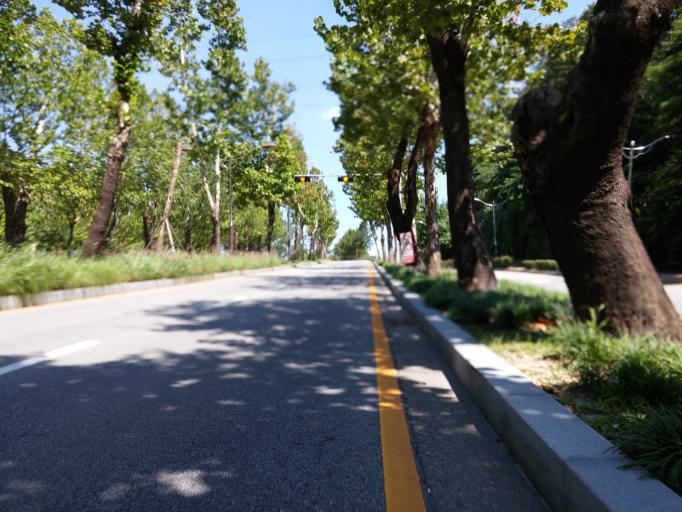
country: KR
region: Chungcheongbuk-do
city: Cheongju-si
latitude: 36.6239
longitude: 127.4087
